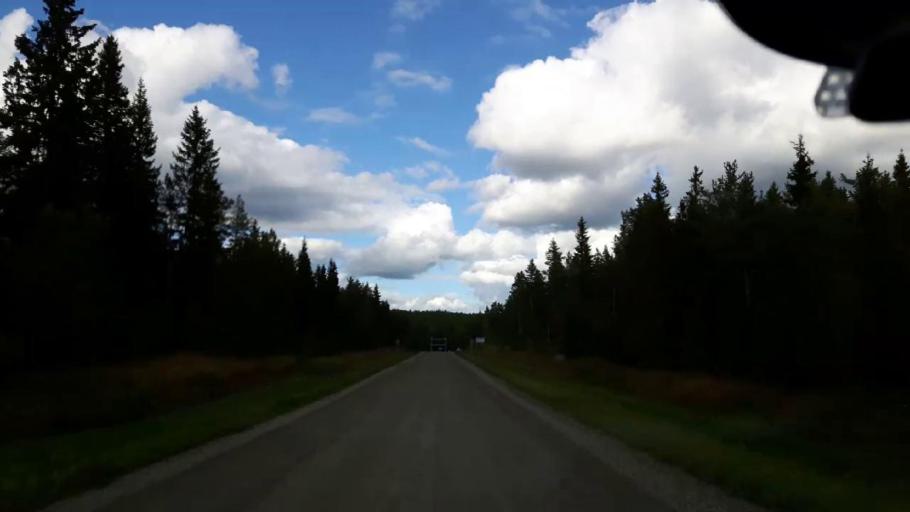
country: SE
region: Jaemtland
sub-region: Stroemsunds Kommun
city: Stroemsund
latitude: 63.4124
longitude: 15.5639
